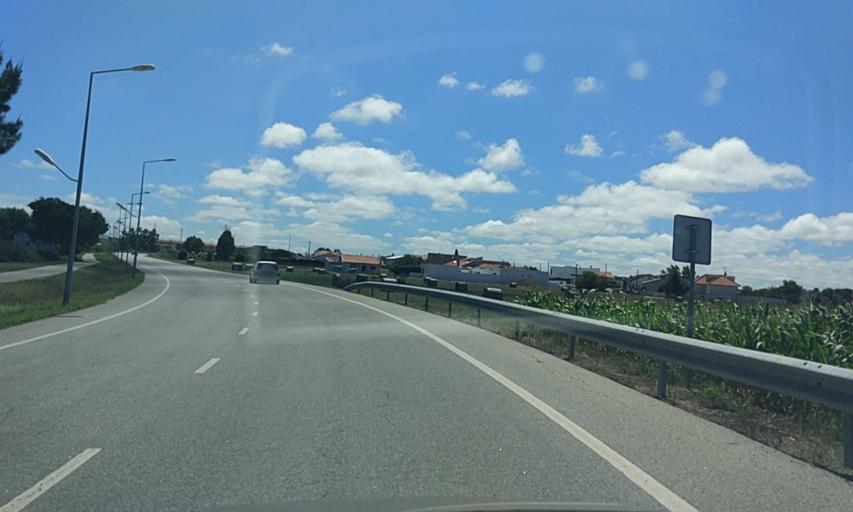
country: PT
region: Aveiro
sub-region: Ilhavo
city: Ilhavo
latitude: 40.6041
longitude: -8.6811
